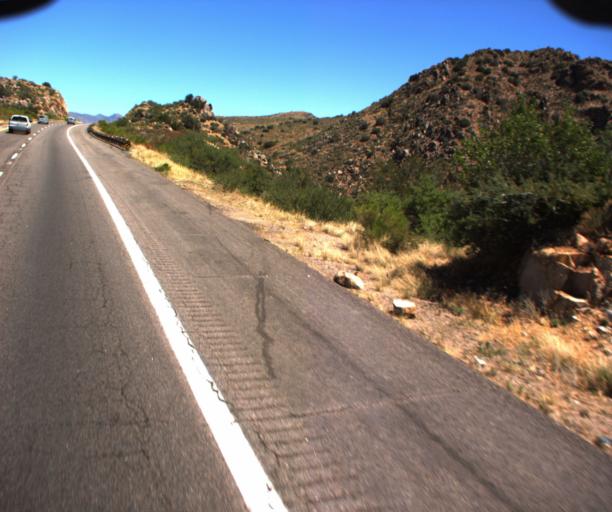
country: US
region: Arizona
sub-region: Gila County
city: Tonto Basin
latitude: 33.8441
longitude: -111.4680
